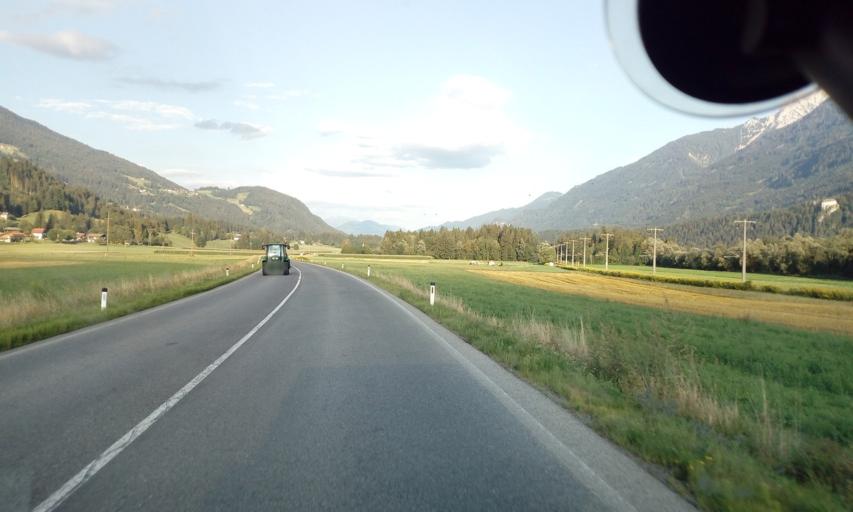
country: AT
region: Carinthia
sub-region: Politischer Bezirk Spittal an der Drau
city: Irschen
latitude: 46.7429
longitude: 13.0028
